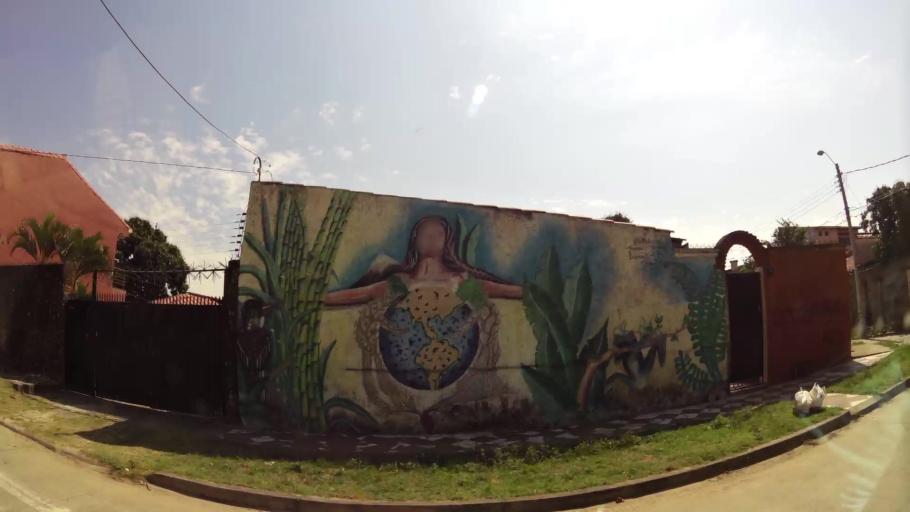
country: BO
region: Santa Cruz
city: Santa Cruz de la Sierra
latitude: -17.7489
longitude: -63.1889
